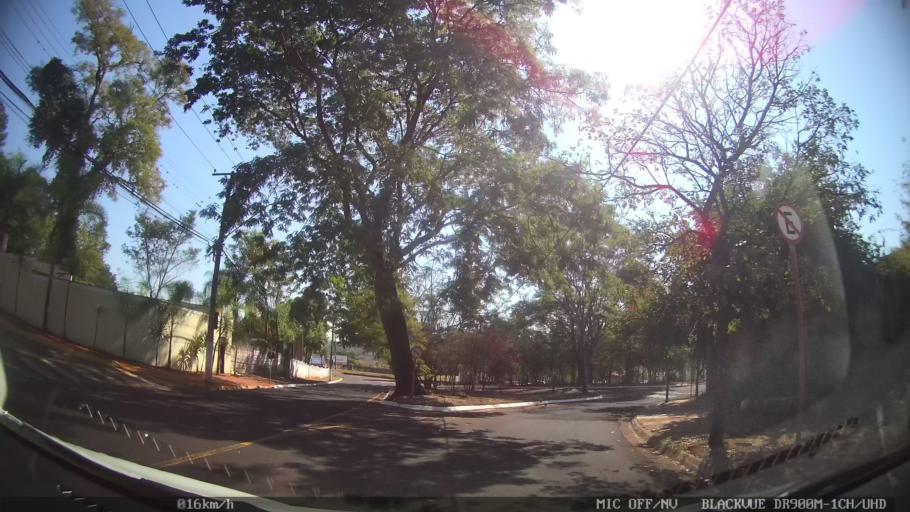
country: BR
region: Sao Paulo
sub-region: Ribeirao Preto
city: Ribeirao Preto
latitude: -21.2115
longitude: -47.7883
